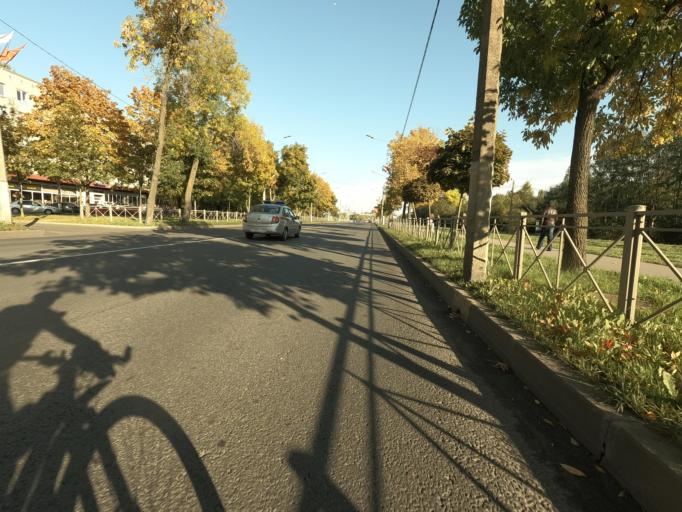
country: RU
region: St.-Petersburg
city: Kolpino
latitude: 59.7407
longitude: 30.5893
